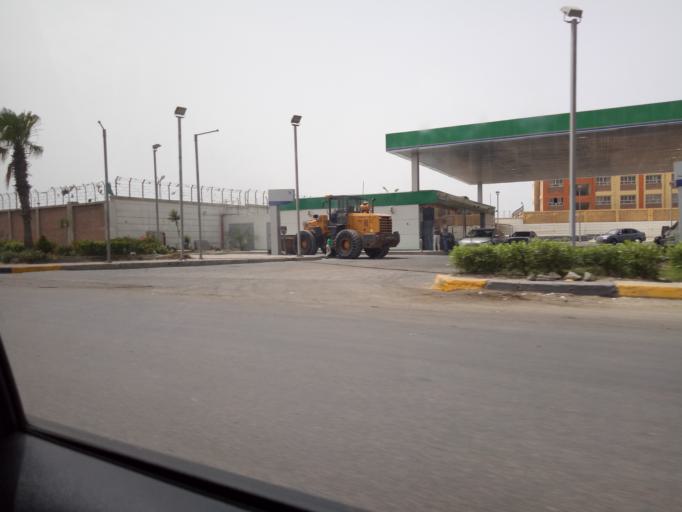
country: EG
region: Alexandria
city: Alexandria
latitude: 31.1449
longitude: 29.8368
